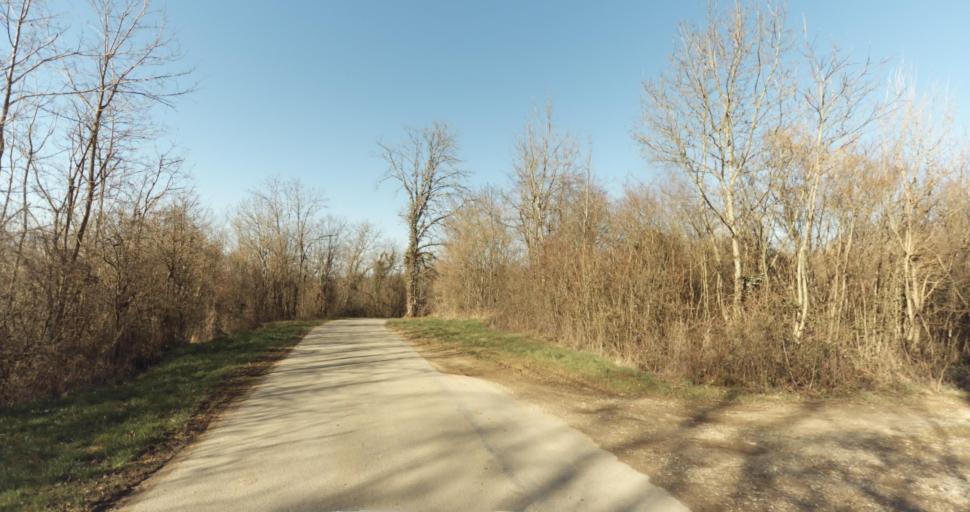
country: FR
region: Franche-Comte
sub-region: Departement du Jura
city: Montmorot
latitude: 46.7016
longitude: 5.5204
